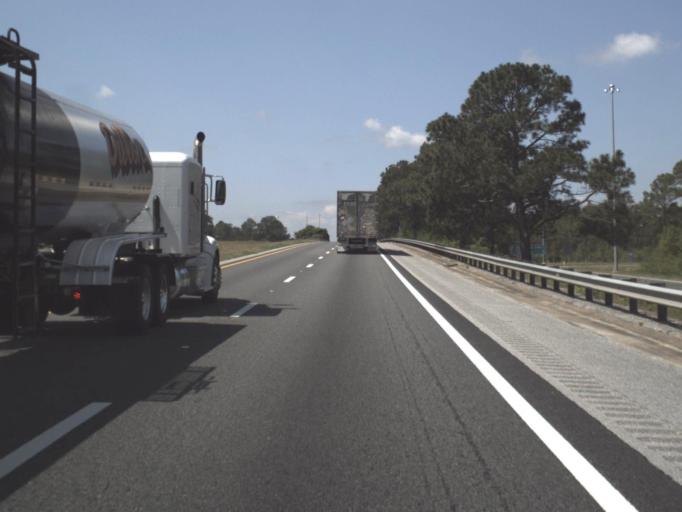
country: US
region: Florida
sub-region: Santa Rosa County
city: Bagdad
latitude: 30.5720
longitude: -87.0290
